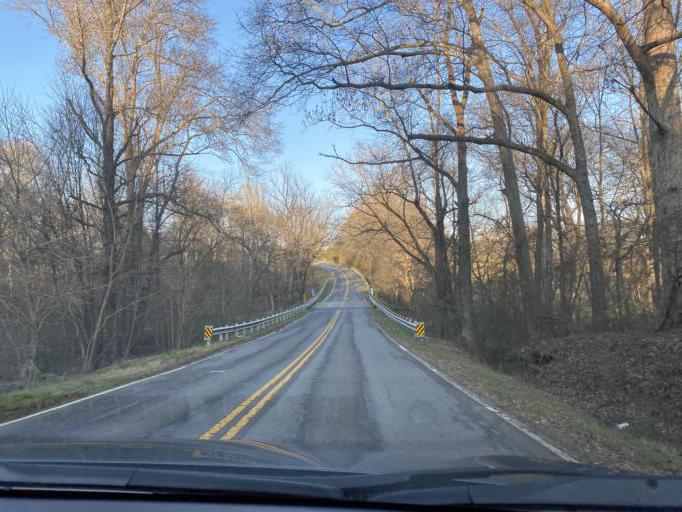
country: US
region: South Carolina
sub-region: Cherokee County
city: East Gaffney
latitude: 35.1119
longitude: -81.6586
